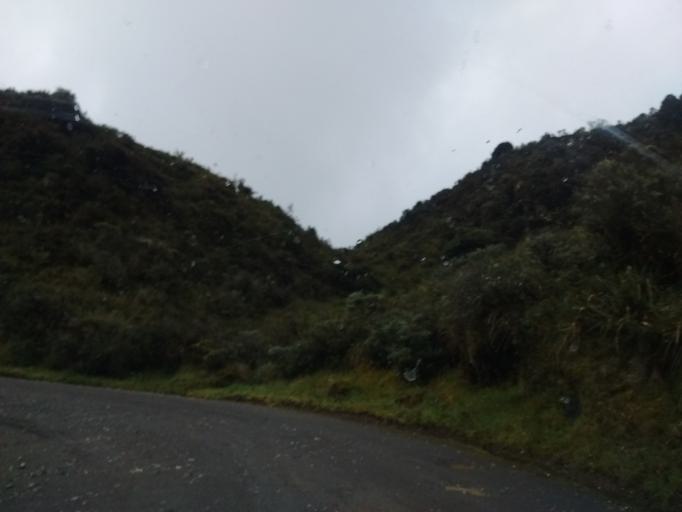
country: CO
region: Cauca
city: Totoro
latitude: 2.3558
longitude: -76.3252
